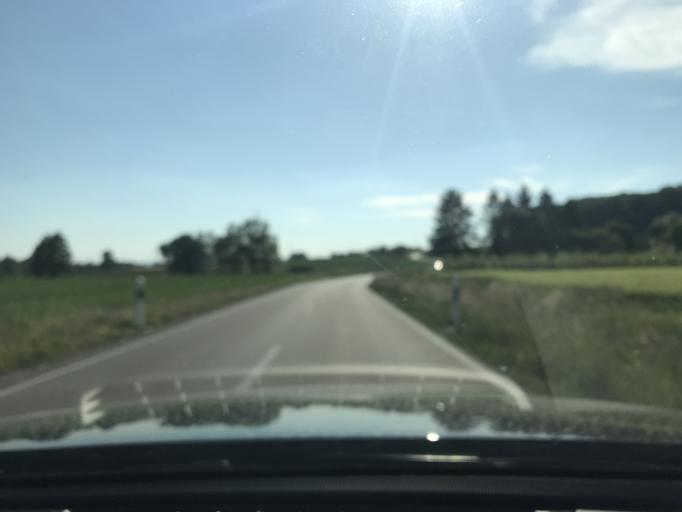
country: DE
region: Baden-Wuerttemberg
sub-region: Regierungsbezirk Stuttgart
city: Schwaikheim
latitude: 48.8926
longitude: 9.3545
